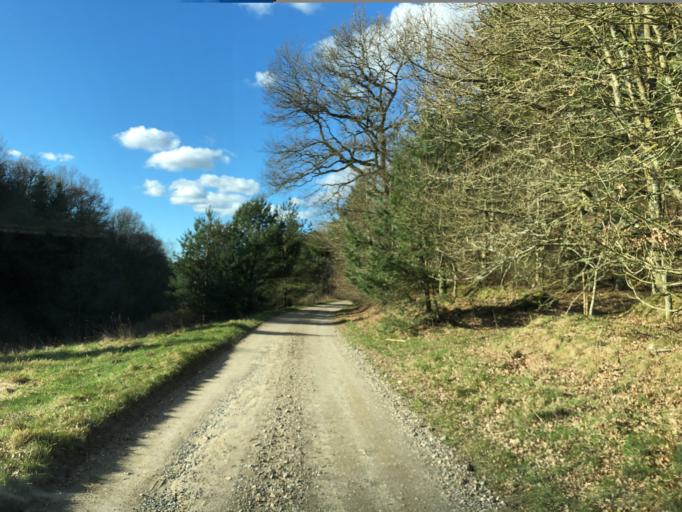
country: DK
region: Central Jutland
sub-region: Favrskov Kommune
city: Hammel
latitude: 56.3129
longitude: 9.9109
